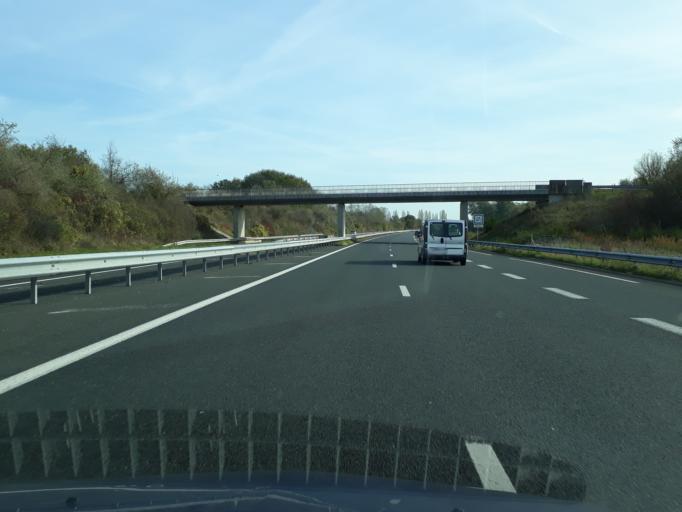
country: FR
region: Champagne-Ardenne
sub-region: Departement de l'Aube
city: Saint-Pouange
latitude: 48.2338
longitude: 4.0428
